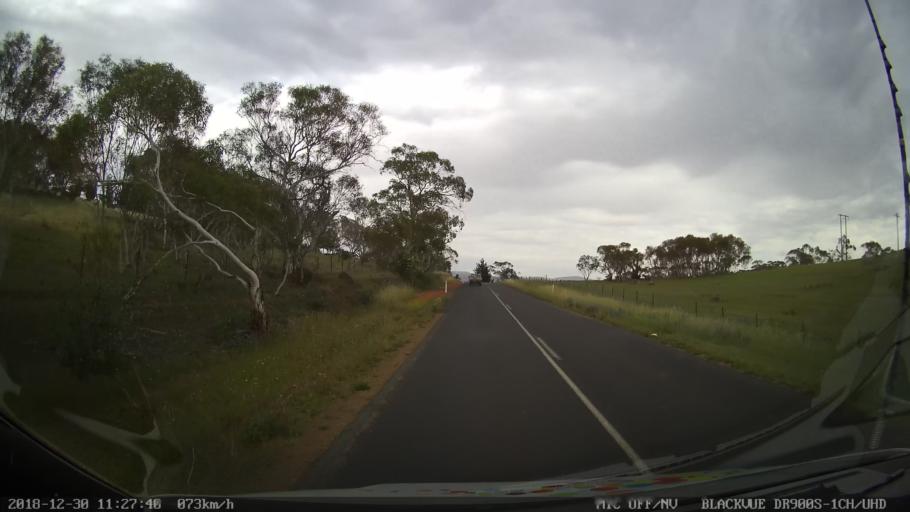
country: AU
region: New South Wales
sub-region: Snowy River
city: Jindabyne
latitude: -36.4585
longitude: 148.6250
